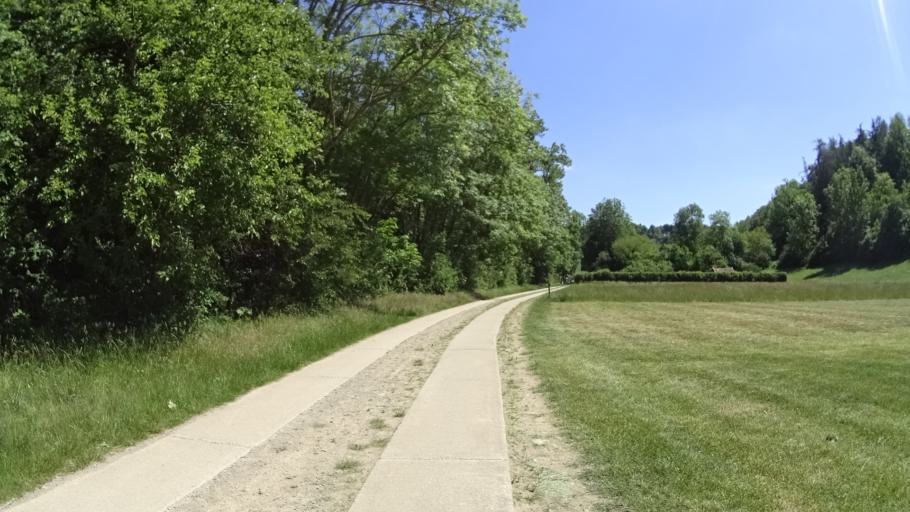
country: DE
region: Bavaria
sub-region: Regierungsbezirk Mittelfranken
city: Rothenburg ob der Tauber
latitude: 49.3833
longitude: 10.1694
